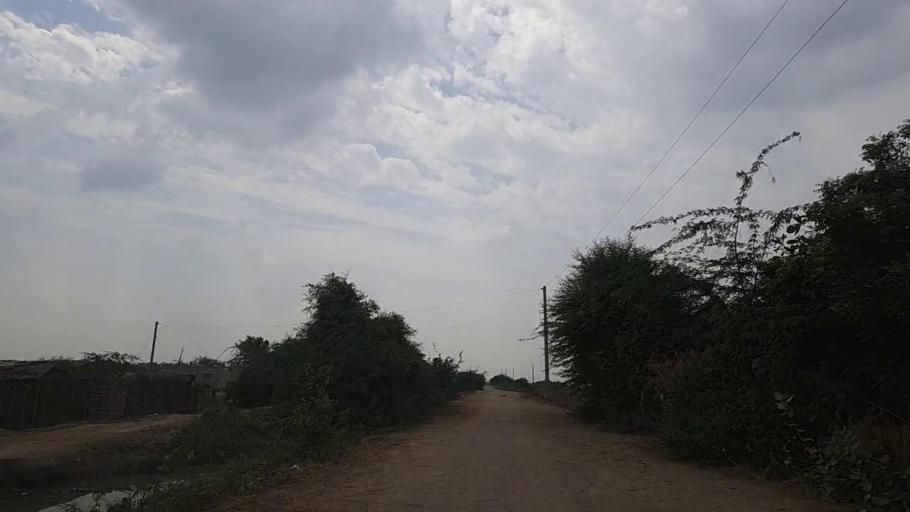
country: PK
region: Sindh
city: Mirpur Batoro
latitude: 24.6224
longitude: 68.1375
